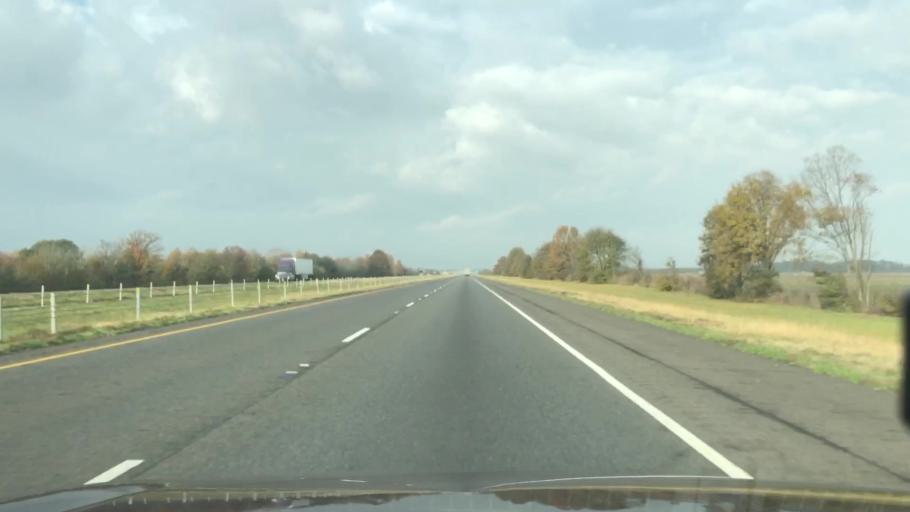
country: US
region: Louisiana
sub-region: Richland Parish
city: Delhi
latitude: 32.4279
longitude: -91.3949
